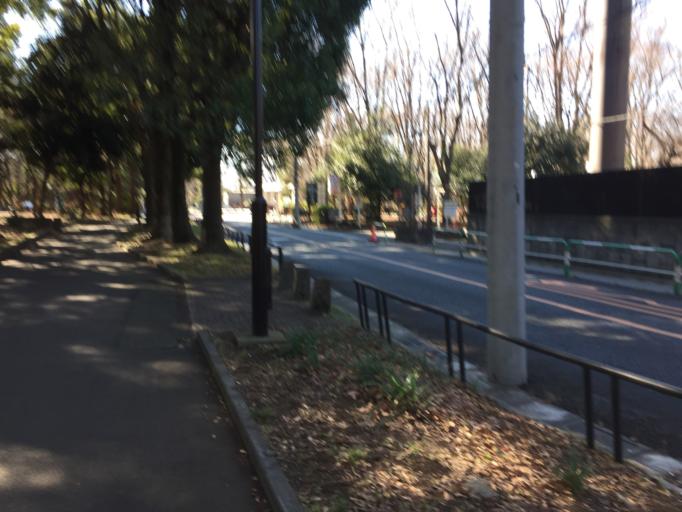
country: JP
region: Tokyo
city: Chofugaoka
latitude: 35.6302
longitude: 139.6150
